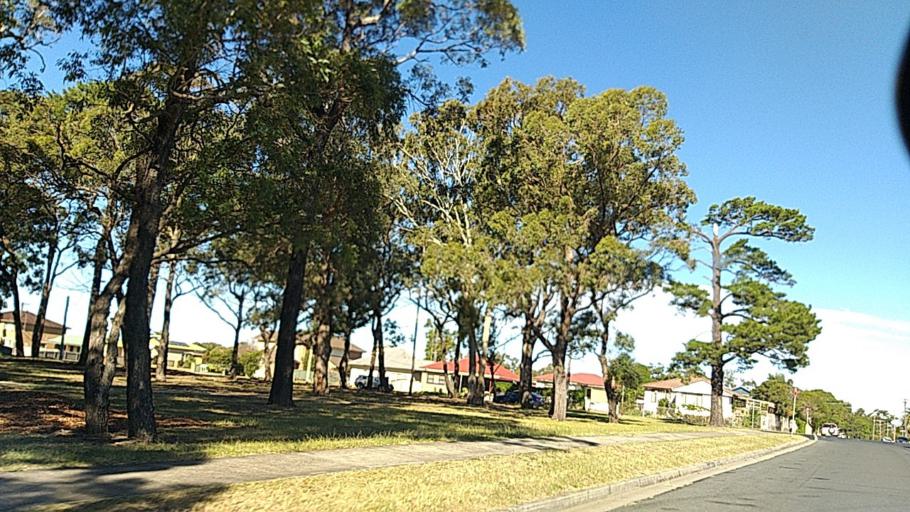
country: AU
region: New South Wales
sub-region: Wollongong
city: East Corrimal
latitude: -34.3750
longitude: 150.9061
